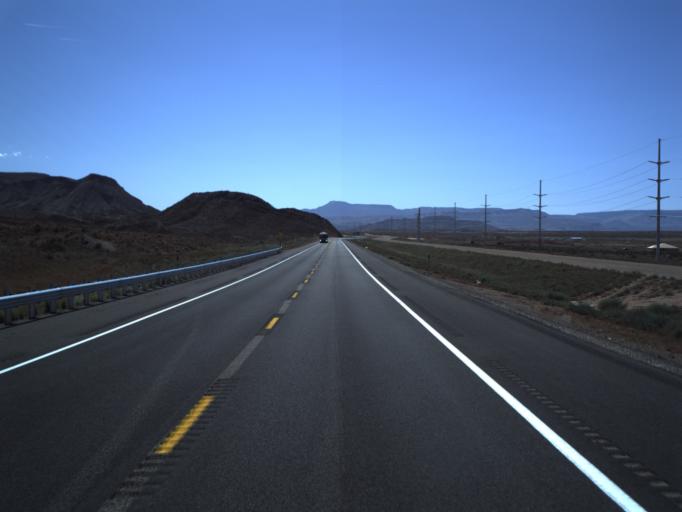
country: US
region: Utah
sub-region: Washington County
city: Washington
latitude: 37.0733
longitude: -113.4858
